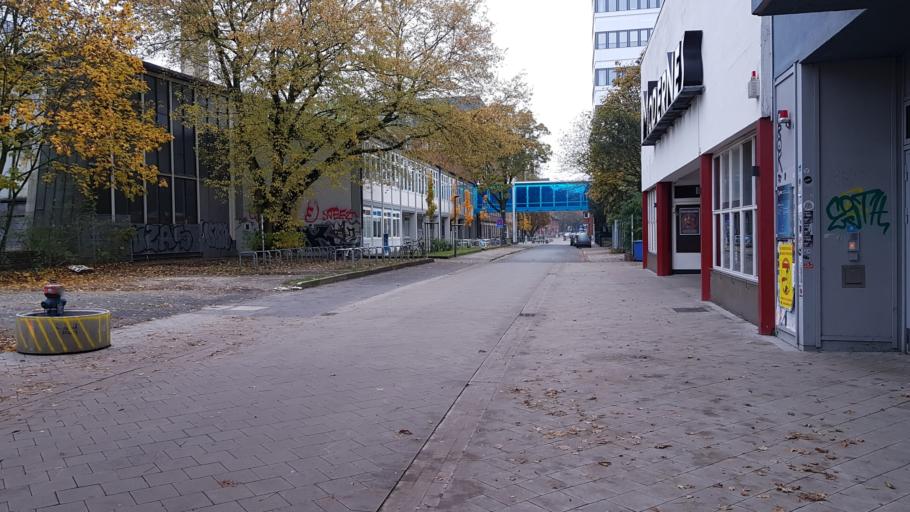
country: DE
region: Bremen
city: Bremen
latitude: 53.0719
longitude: 8.7946
